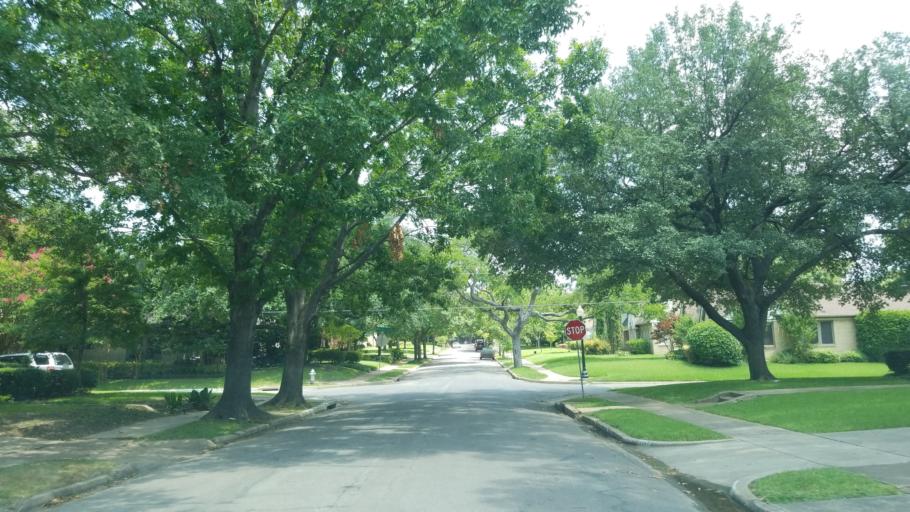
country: US
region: Texas
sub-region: Dallas County
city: Highland Park
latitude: 32.8291
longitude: -96.7727
